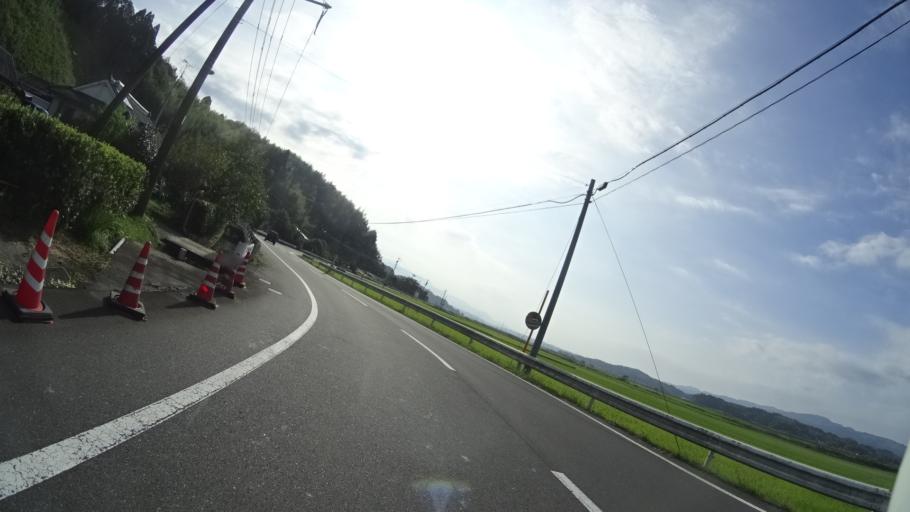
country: JP
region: Kagoshima
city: Okuchi-shinohara
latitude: 32.0244
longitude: 130.6047
